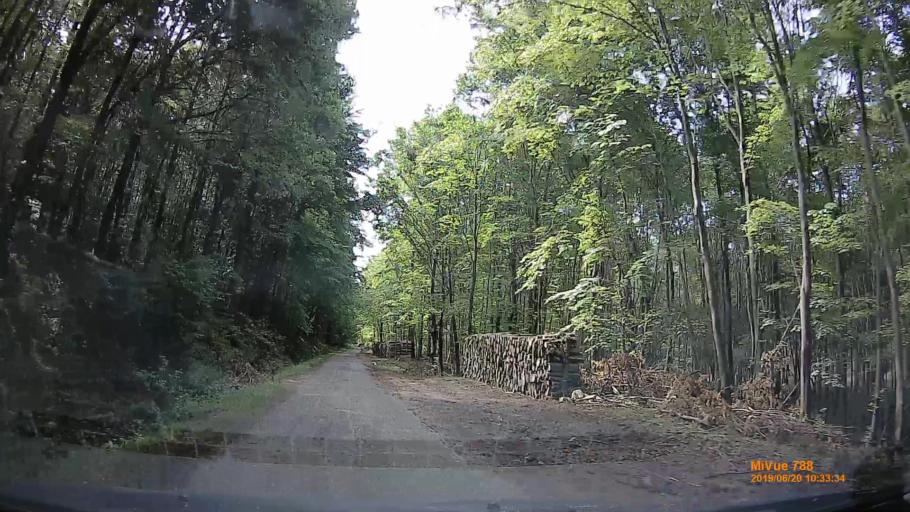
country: HU
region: Baranya
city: Mecseknadasd
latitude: 46.2030
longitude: 18.5164
